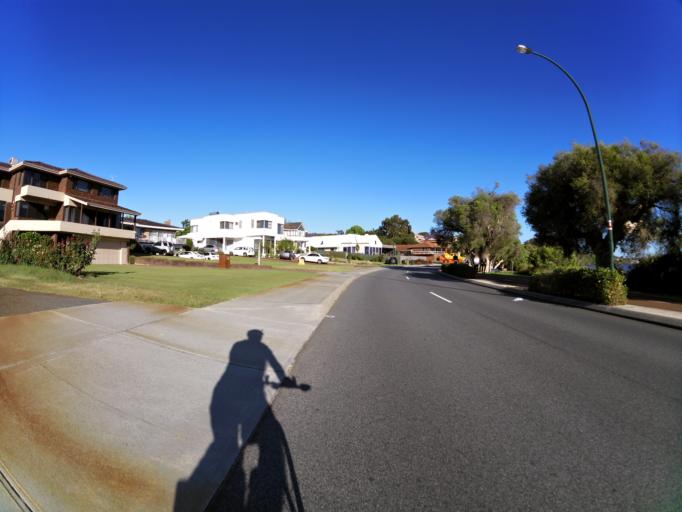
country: AU
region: Western Australia
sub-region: Melville
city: Mount Pleasant
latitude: -32.0357
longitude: 115.8548
